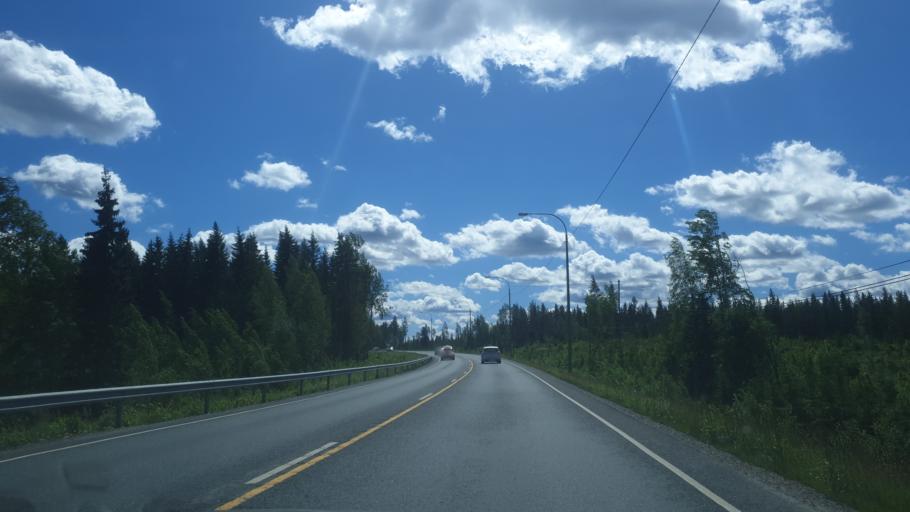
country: FI
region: Northern Savo
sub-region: Varkaus
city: Leppaevirta
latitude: 62.5706
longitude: 27.6102
